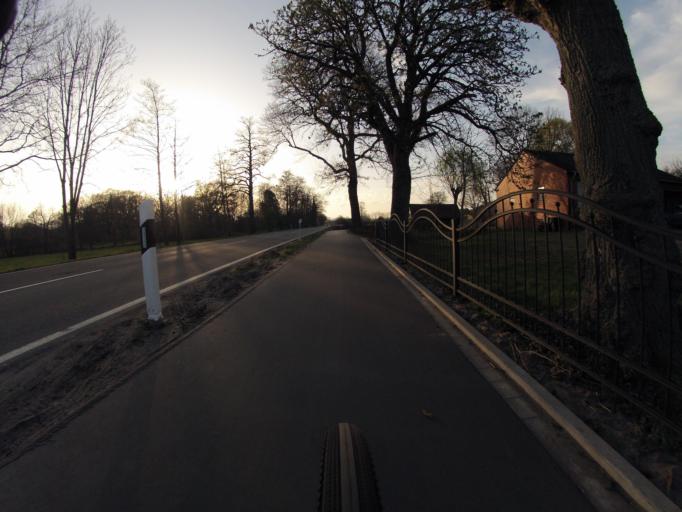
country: DE
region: North Rhine-Westphalia
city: Ibbenburen
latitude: 52.2305
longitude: 7.7114
